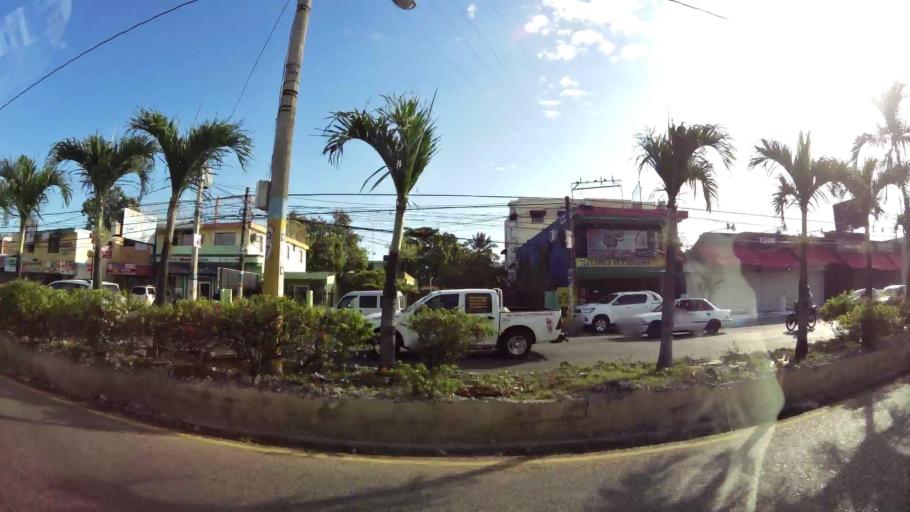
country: DO
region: Santo Domingo
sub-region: Santo Domingo
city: Santo Domingo Este
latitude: 18.5038
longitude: -69.8557
